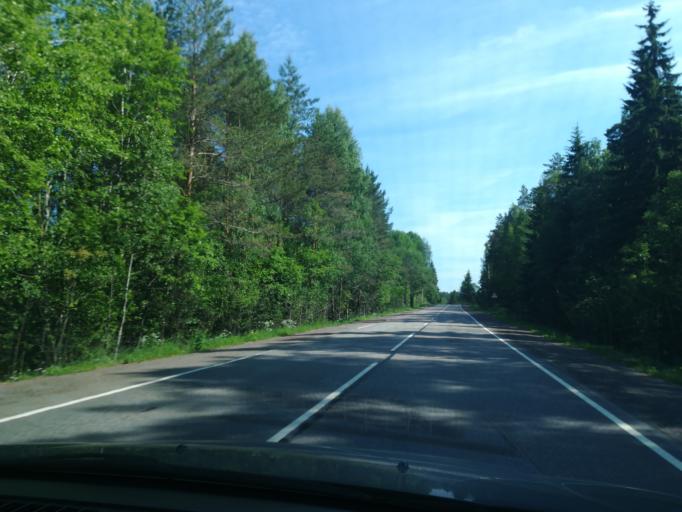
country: RU
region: Leningrad
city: Lesogorskiy
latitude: 60.9386
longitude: 28.8914
